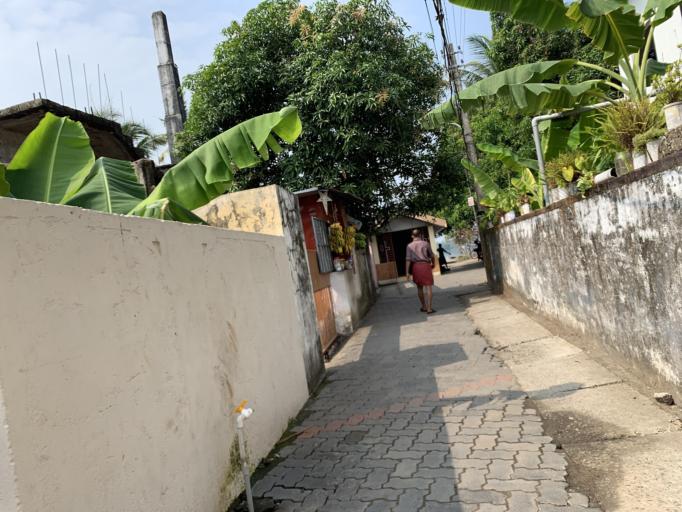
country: IN
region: Kerala
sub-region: Ernakulam
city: Cochin
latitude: 9.8960
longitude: 76.2947
